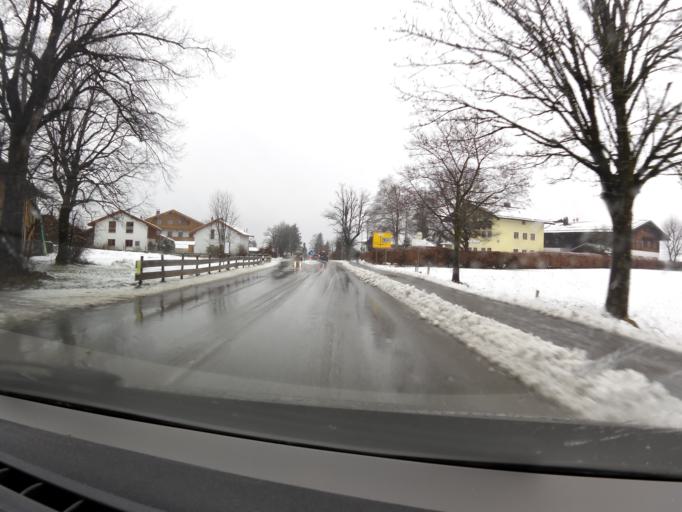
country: DE
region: Bavaria
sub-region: Upper Bavaria
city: Waakirchen
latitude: 47.7696
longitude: 11.6778
